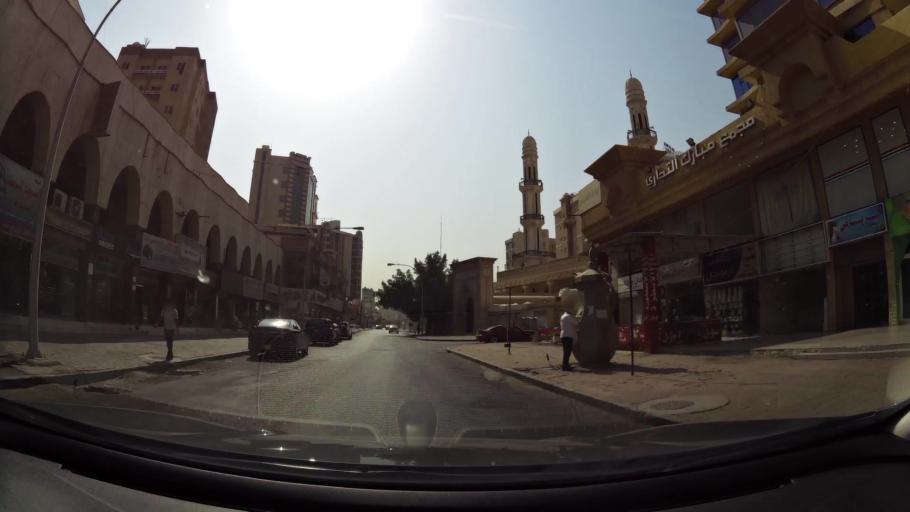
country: KW
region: Muhafazat Hawalli
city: Hawalli
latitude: 29.3448
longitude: 48.0122
